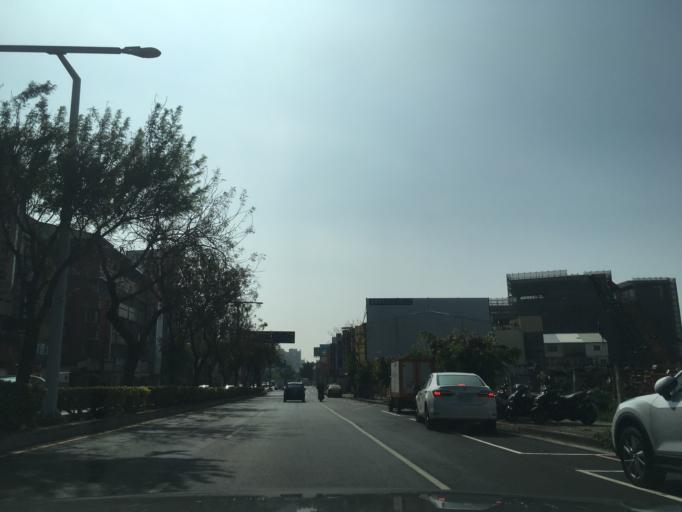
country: TW
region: Taiwan
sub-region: Taichung City
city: Taichung
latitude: 24.1946
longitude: 120.6587
